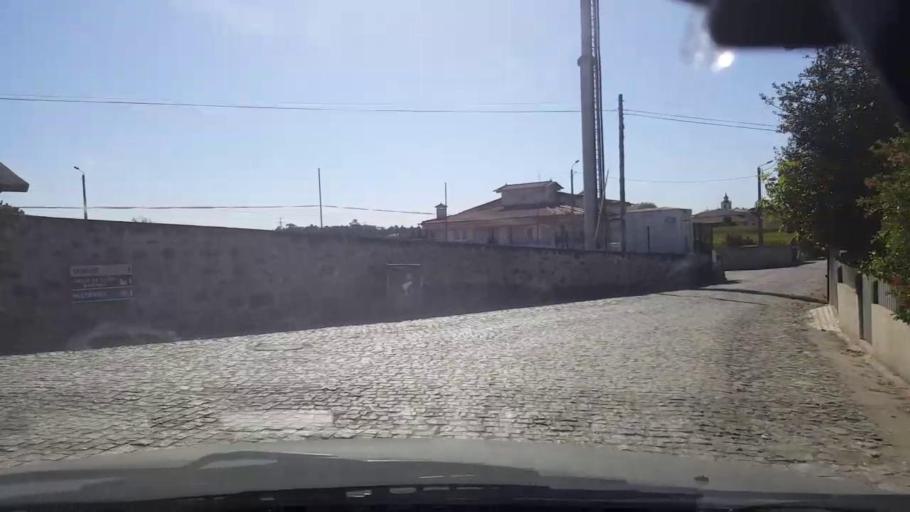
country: PT
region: Braga
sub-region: Vila Nova de Famalicao
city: Ribeirao
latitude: 41.3563
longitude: -8.6281
